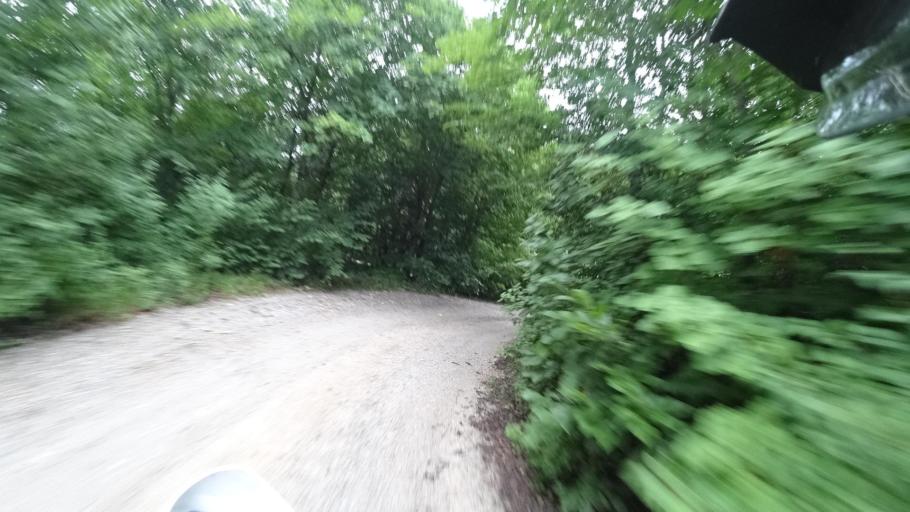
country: BA
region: Federation of Bosnia and Herzegovina
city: Orasac
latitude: 44.4918
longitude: 15.9695
